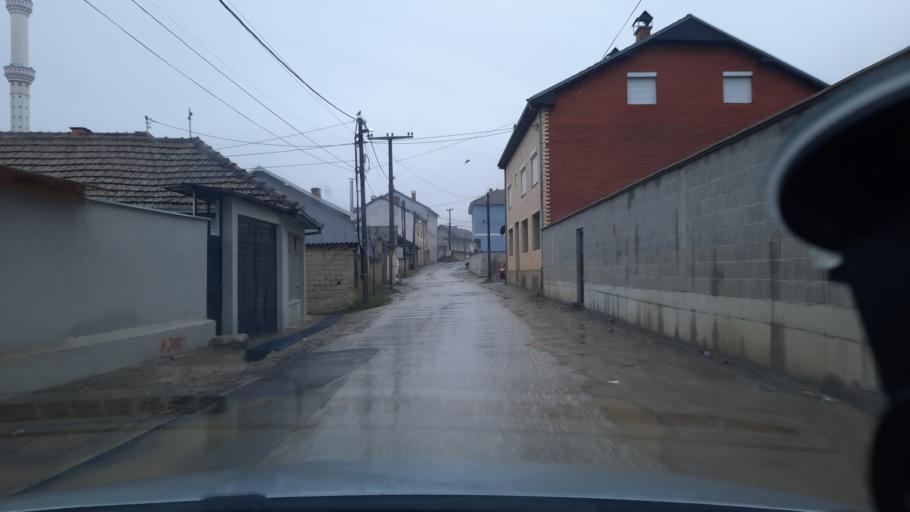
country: MK
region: Opstina Lipkovo
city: Lipkovo
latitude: 42.1573
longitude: 21.5840
